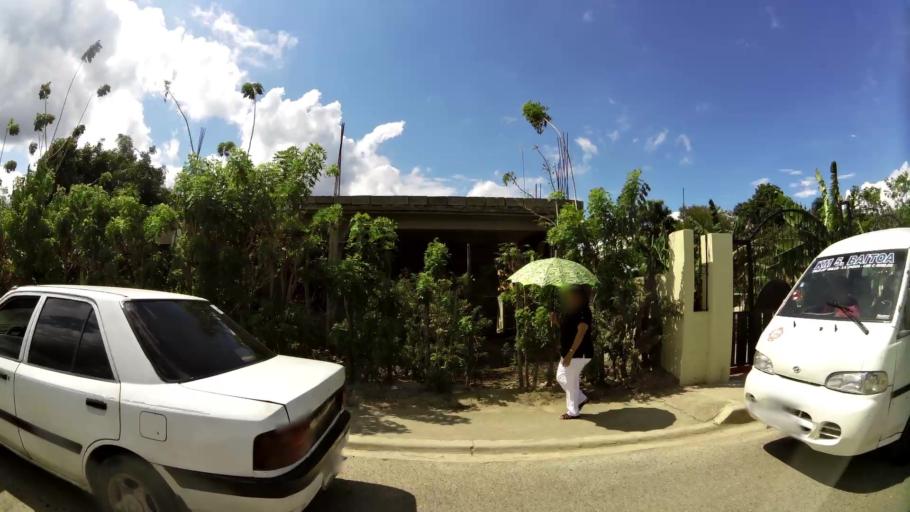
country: DO
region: Santiago
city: Licey al Medio
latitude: 19.3810
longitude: -70.6141
